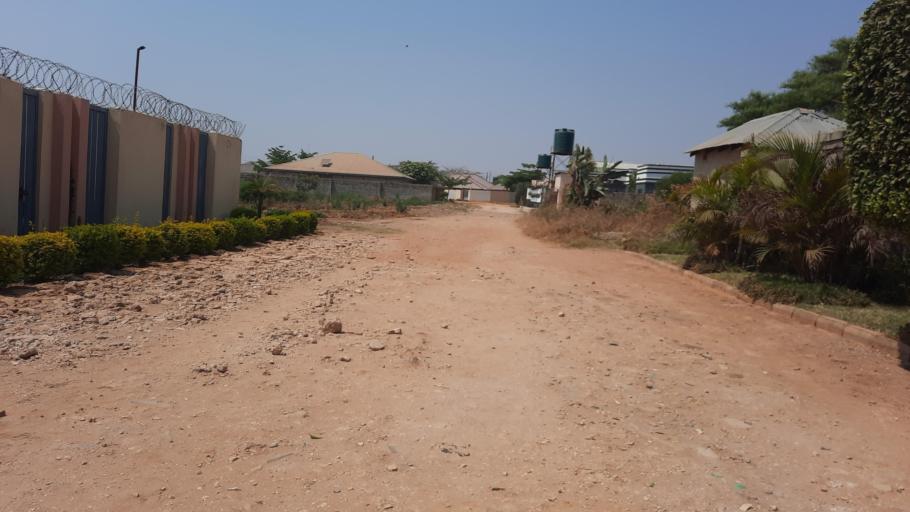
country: ZM
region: Lusaka
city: Lusaka
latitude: -15.3928
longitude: 28.3912
